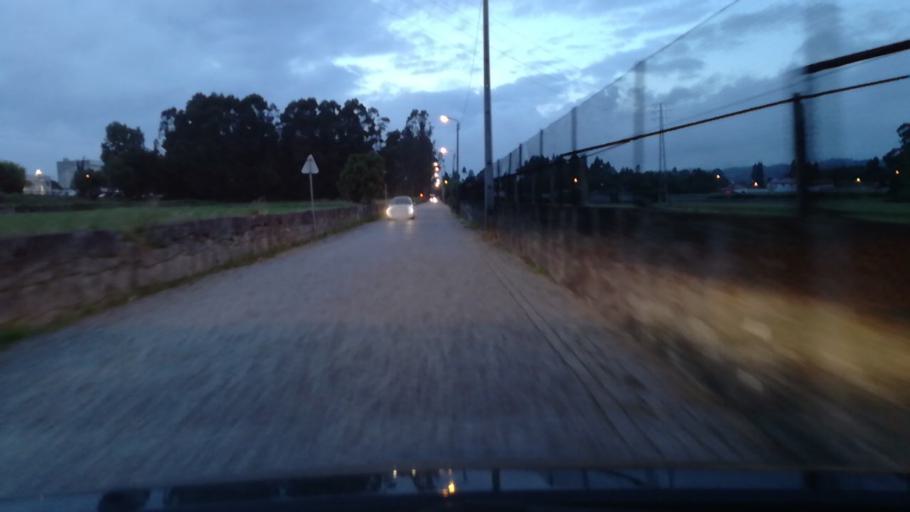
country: PT
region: Porto
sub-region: Maia
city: Anta
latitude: 41.2569
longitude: -8.6086
